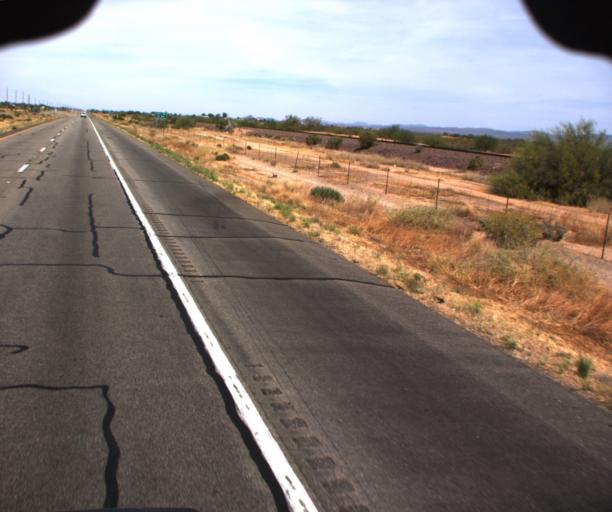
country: US
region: Arizona
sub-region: Maricopa County
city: Sun City West
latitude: 33.7636
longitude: -112.5100
